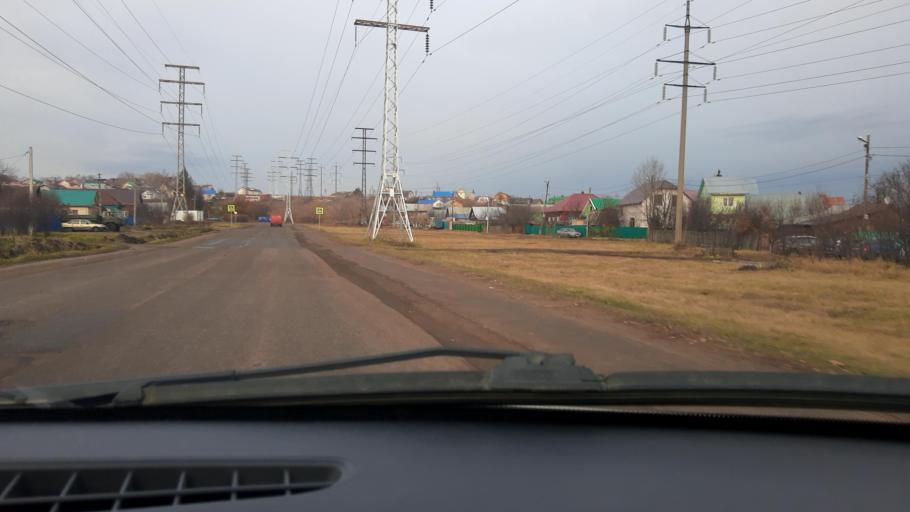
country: RU
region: Bashkortostan
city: Avdon
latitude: 54.6937
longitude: 55.8159
